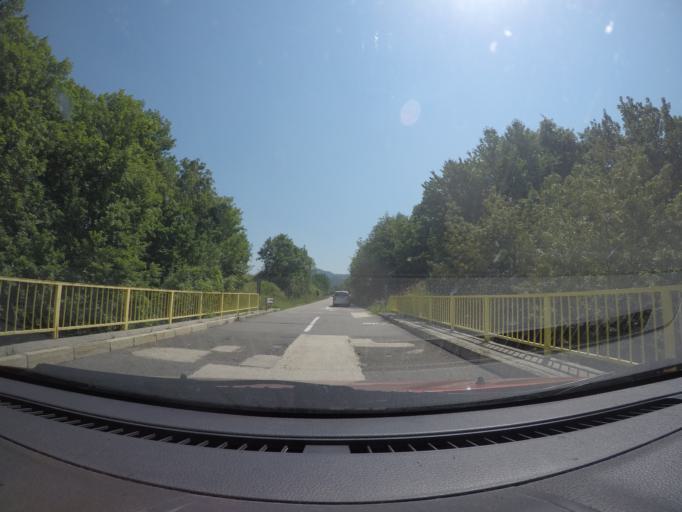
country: RO
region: Mehedinti
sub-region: Comuna Eselnita
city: Eselnita
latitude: 44.6682
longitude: 22.3666
